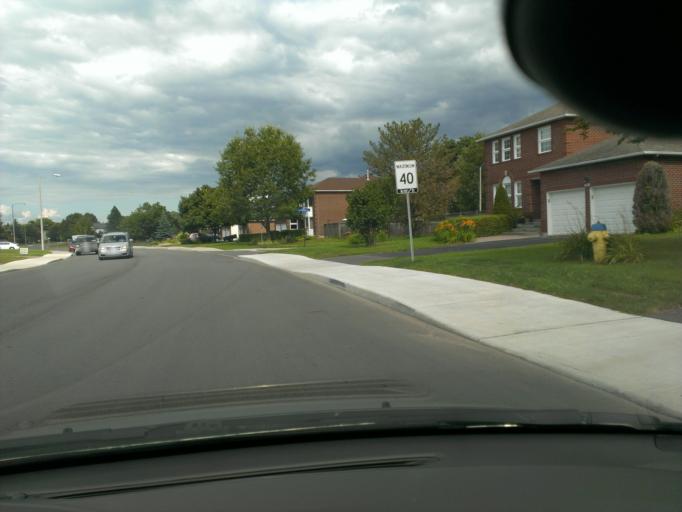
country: CA
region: Quebec
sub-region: Outaouais
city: Gatineau
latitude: 45.4837
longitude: -75.4923
